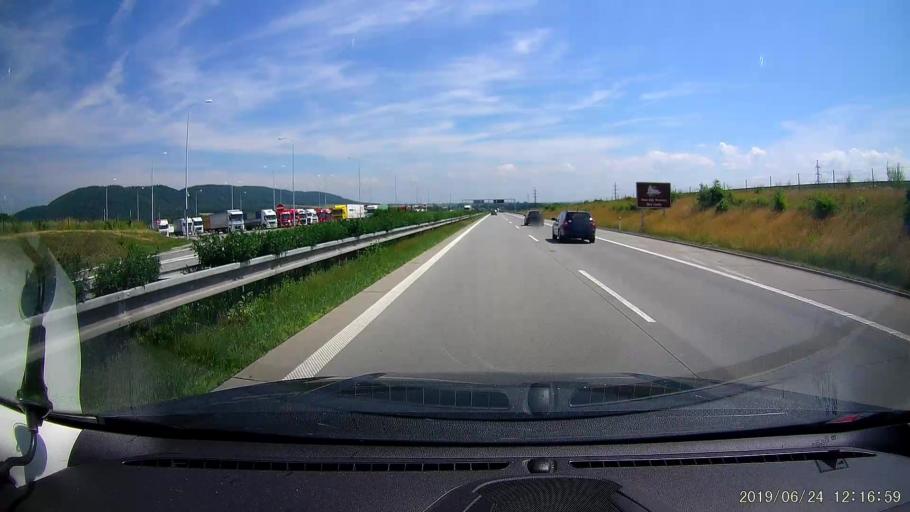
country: CZ
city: Odry
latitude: 49.6303
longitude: 17.8409
